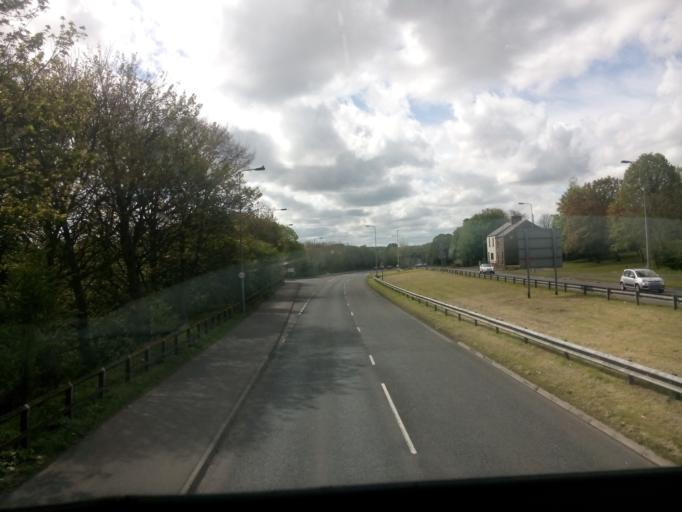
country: GB
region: England
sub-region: County Durham
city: Sacriston
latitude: 54.8235
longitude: -1.5929
